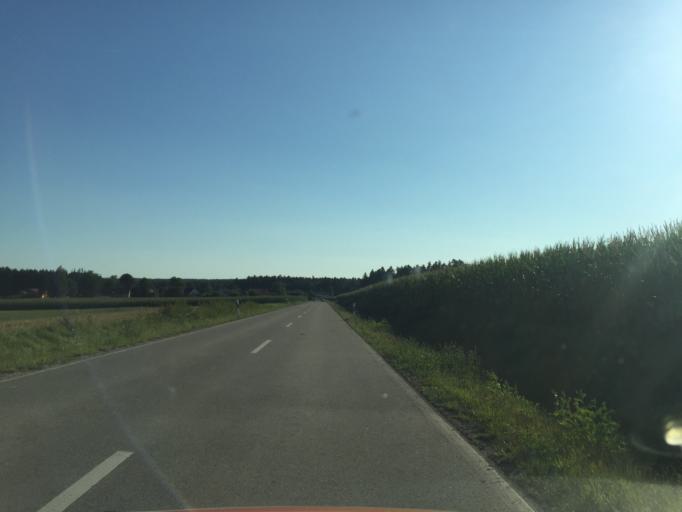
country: DE
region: Bavaria
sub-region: Upper Palatinate
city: Grafenwohr
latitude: 49.7581
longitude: 11.8993
